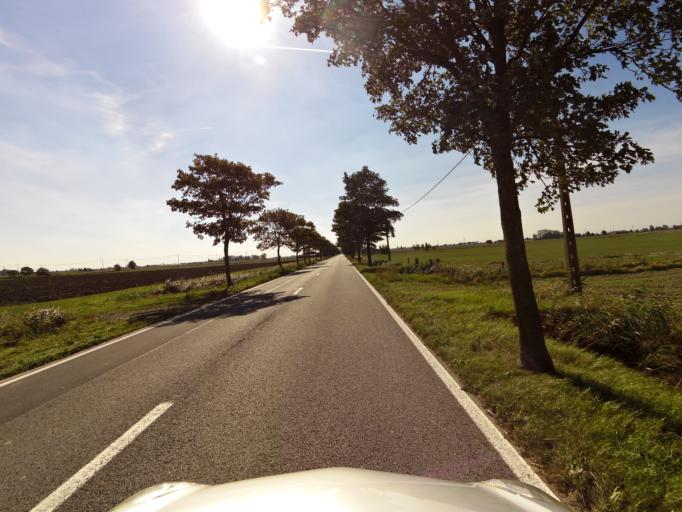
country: BE
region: Flanders
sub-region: Provincie West-Vlaanderen
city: Nieuwpoort
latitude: 51.0917
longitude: 2.8159
